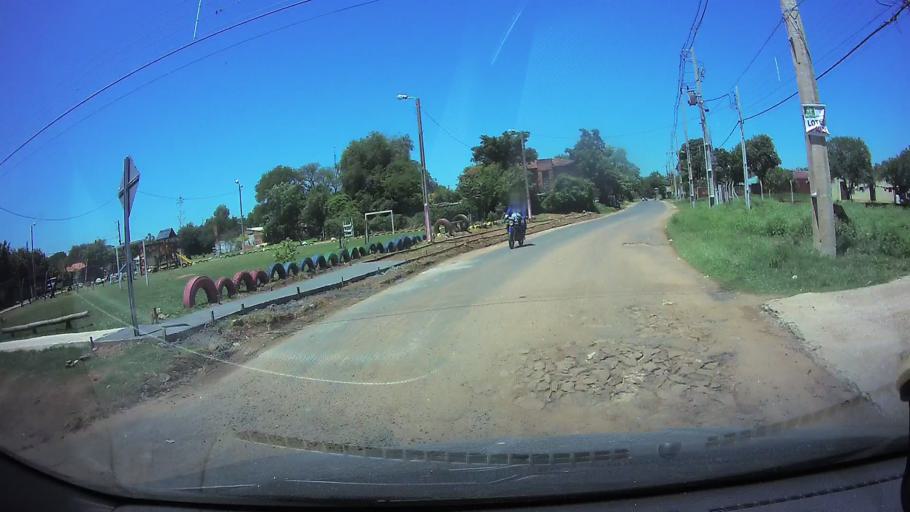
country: PY
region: Central
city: San Lorenzo
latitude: -25.3246
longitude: -57.4829
